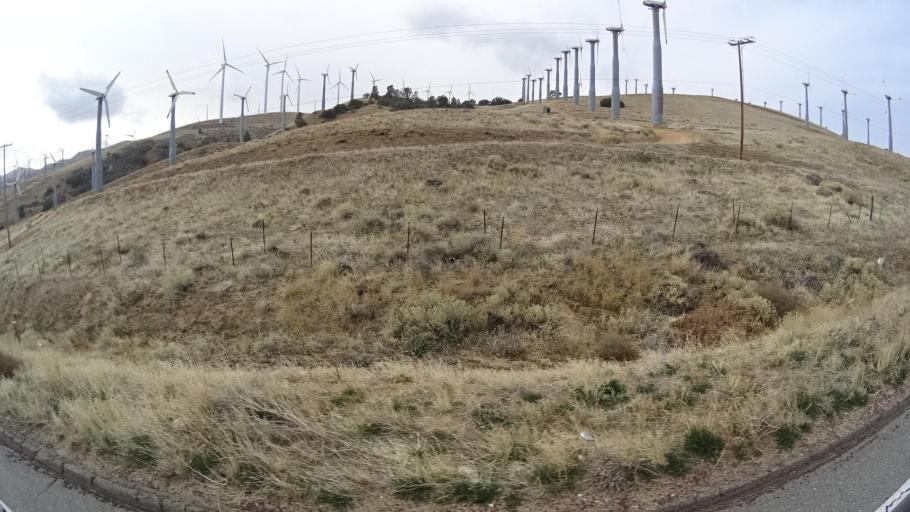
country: US
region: California
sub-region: Kern County
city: Tehachapi
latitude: 35.0591
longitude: -118.3861
